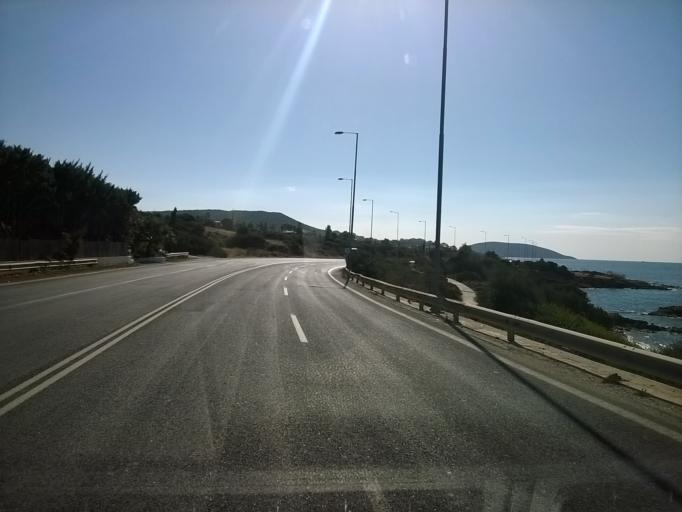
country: GR
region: Attica
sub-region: Nomarchia Anatolikis Attikis
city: Saronida
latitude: 37.7622
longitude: 23.9024
